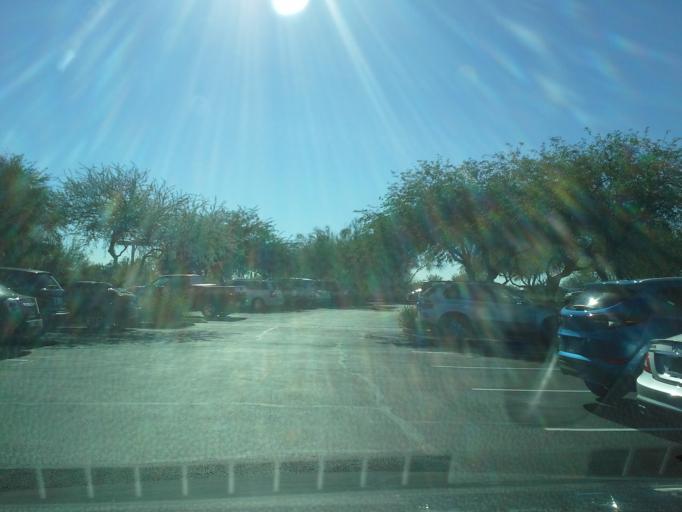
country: US
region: Arizona
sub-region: Maricopa County
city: Carefree
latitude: 33.6774
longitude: -111.8971
